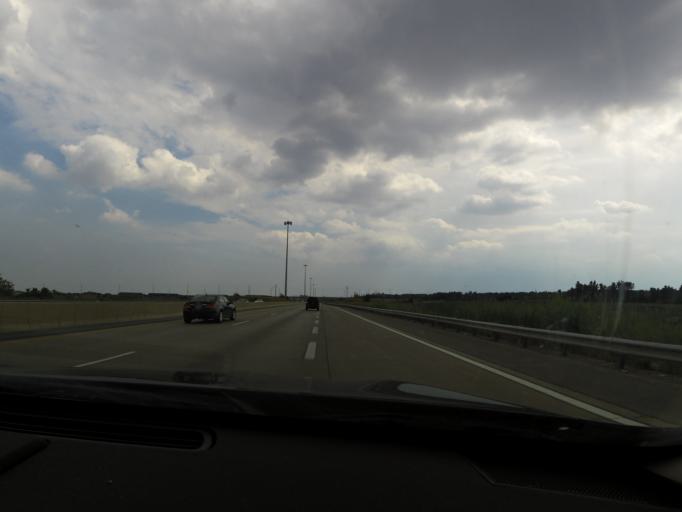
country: CA
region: Ontario
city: Brampton
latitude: 43.7526
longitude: -79.7920
